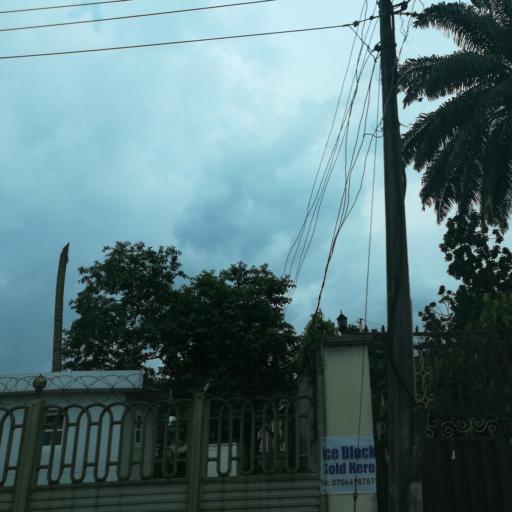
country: NG
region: Rivers
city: Port Harcourt
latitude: 4.8249
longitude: 6.9982
